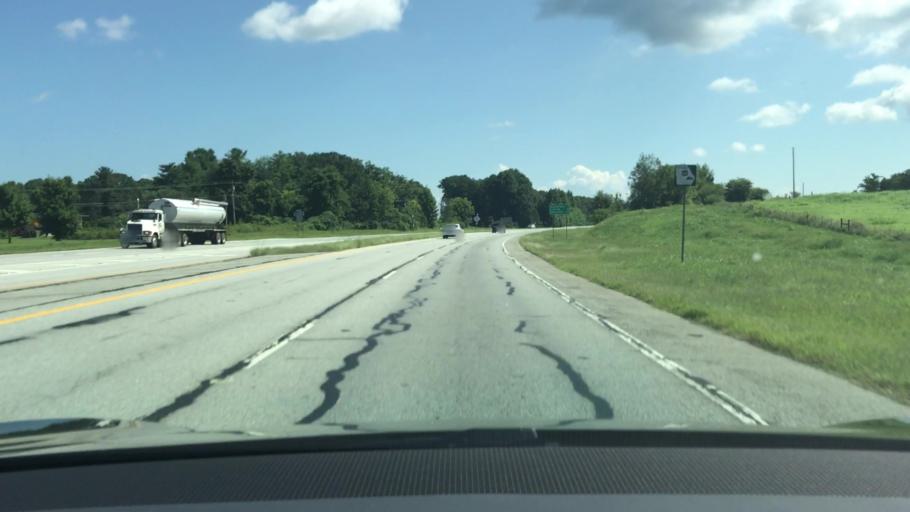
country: US
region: Georgia
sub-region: Habersham County
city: Clarkesville
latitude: 34.6474
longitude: -83.4487
